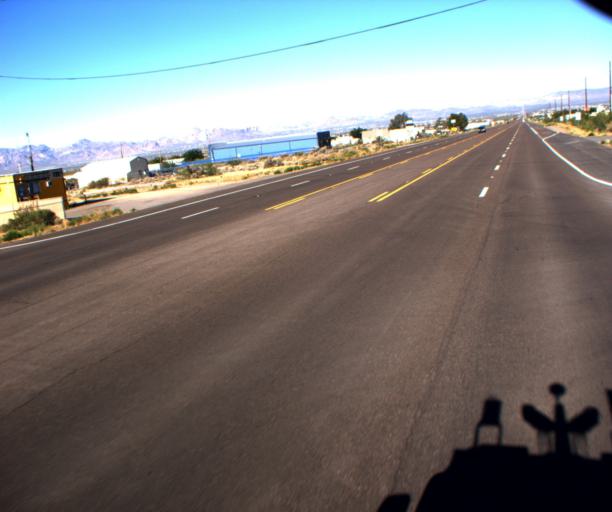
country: US
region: Arizona
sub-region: Mohave County
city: Golden Valley
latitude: 35.2199
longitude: -114.1719
